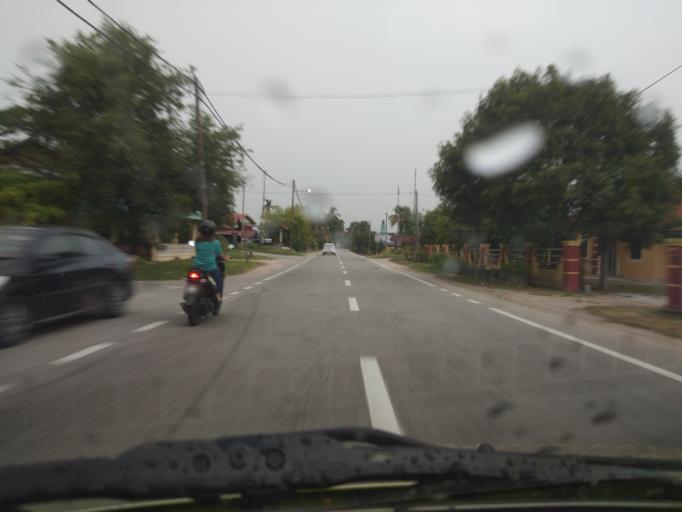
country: MY
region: Penang
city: Permatang Kuching
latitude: 5.4869
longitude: 100.4003
